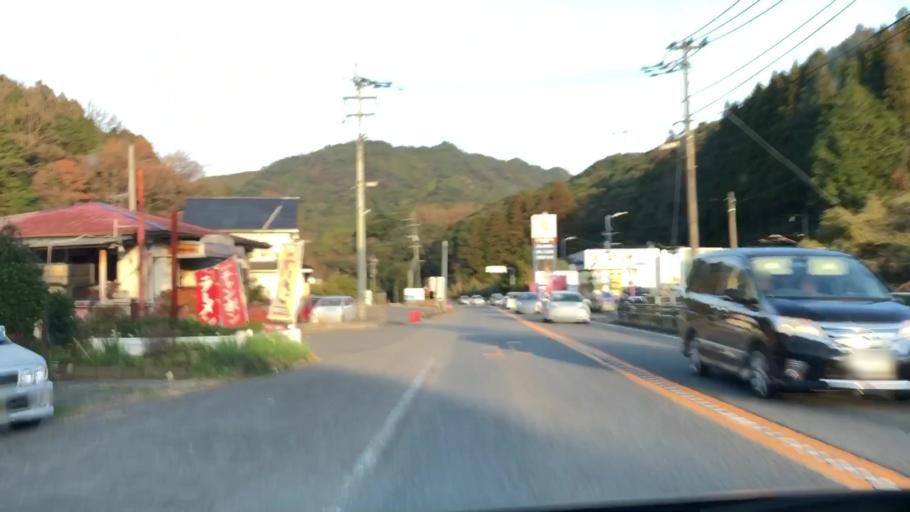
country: JP
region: Kumamoto
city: Minamata
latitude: 32.2141
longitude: 130.4333
